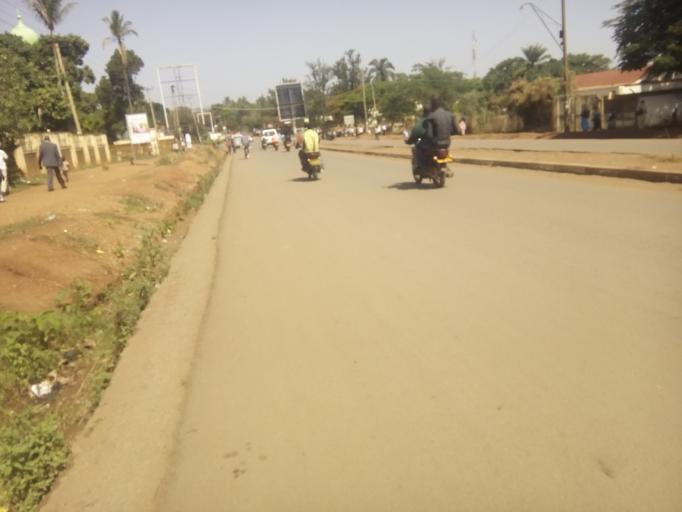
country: UG
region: Eastern Region
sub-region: Mbale District
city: Mbale
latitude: 1.0758
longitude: 34.1759
